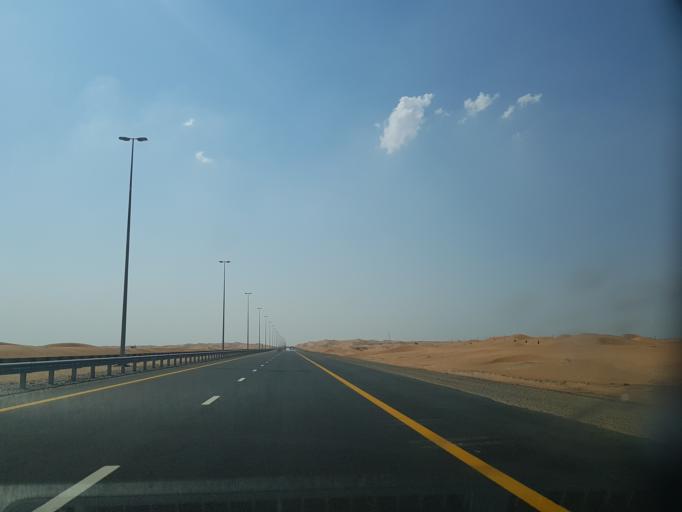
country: AE
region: Ash Shariqah
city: Adh Dhayd
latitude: 25.2571
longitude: 55.7177
